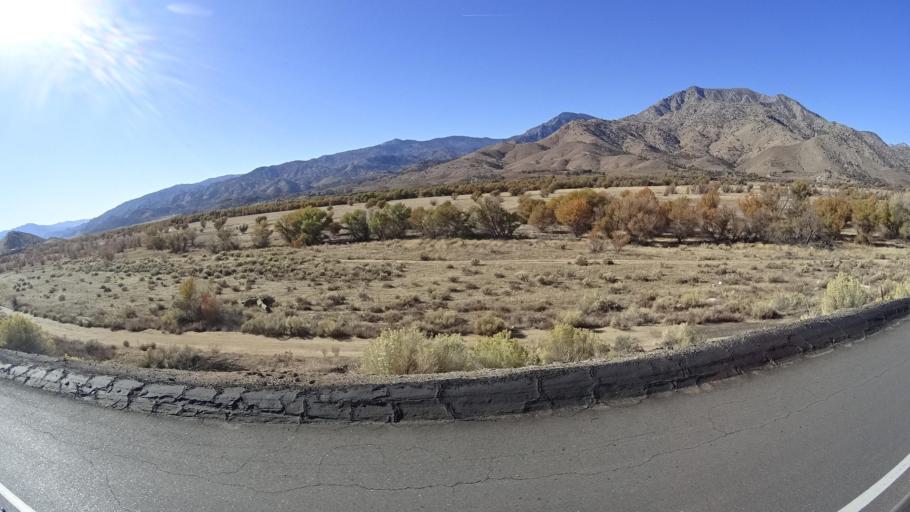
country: US
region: California
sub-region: Kern County
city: Kernville
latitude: 35.7169
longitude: -118.4180
